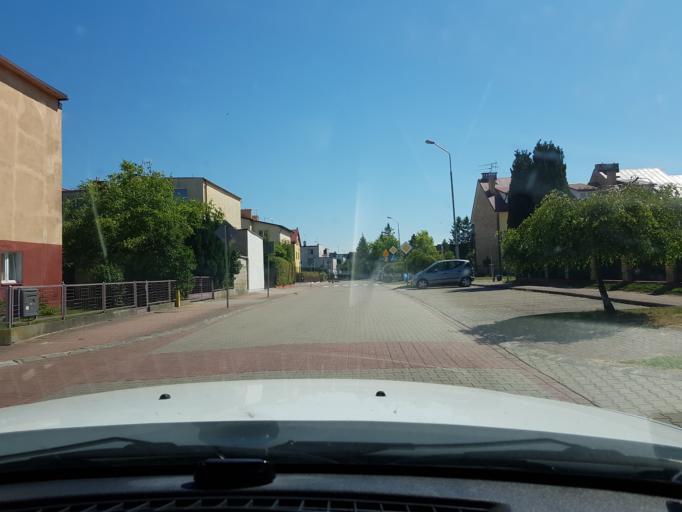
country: PL
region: West Pomeranian Voivodeship
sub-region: Powiat koszalinski
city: Mielno
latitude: 54.2543
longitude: 16.0597
